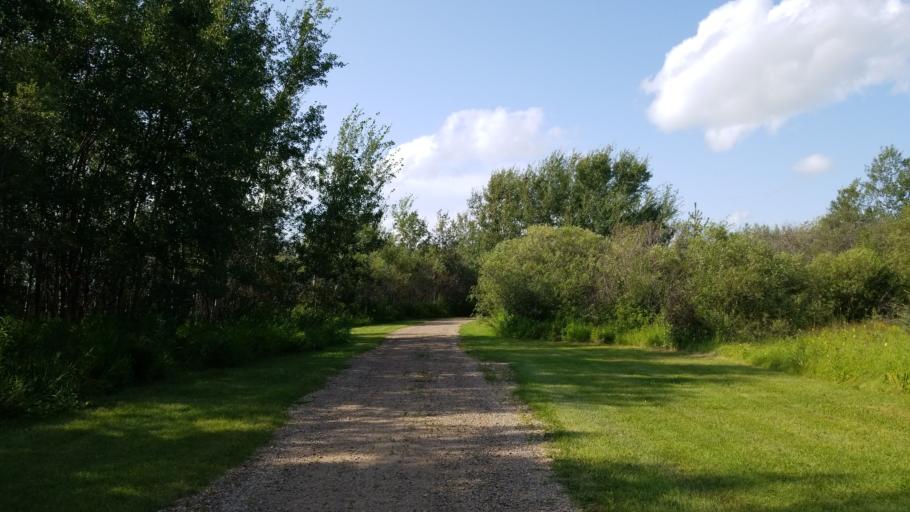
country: CA
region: Saskatchewan
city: Lloydminster
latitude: 53.2572
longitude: -110.0475
